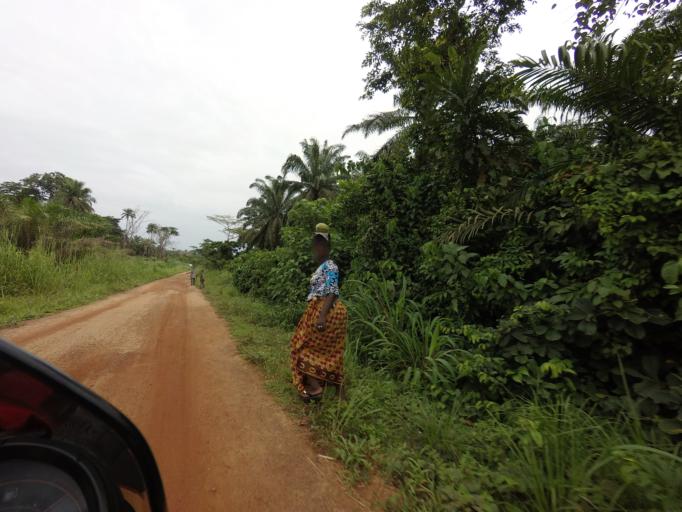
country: SL
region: Eastern Province
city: Mobai
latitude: 7.9362
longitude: -10.7548
